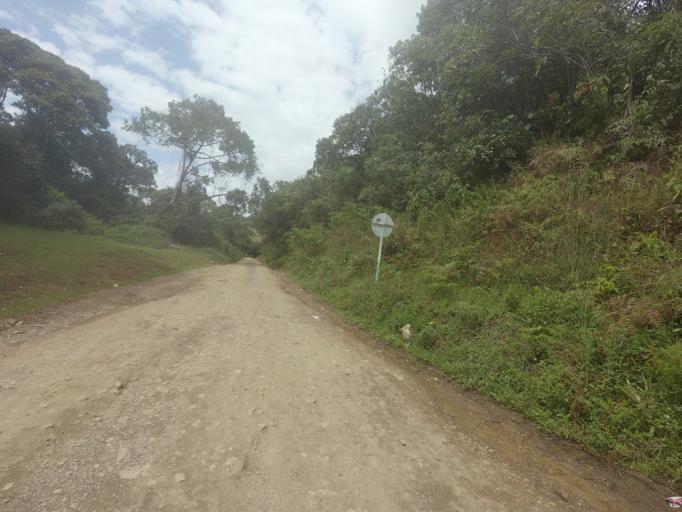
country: CO
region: Huila
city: San Agustin
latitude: 1.8880
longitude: -76.2950
